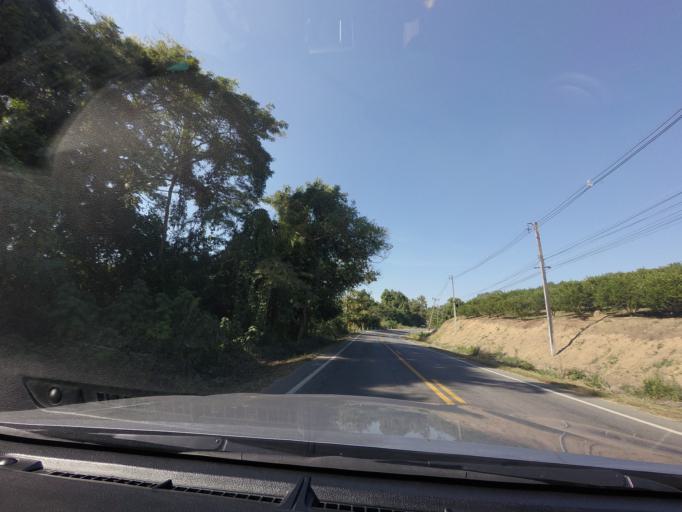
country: TH
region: Sukhothai
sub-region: Amphoe Si Satchanalai
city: Si Satchanalai
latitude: 17.6202
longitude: 99.7058
